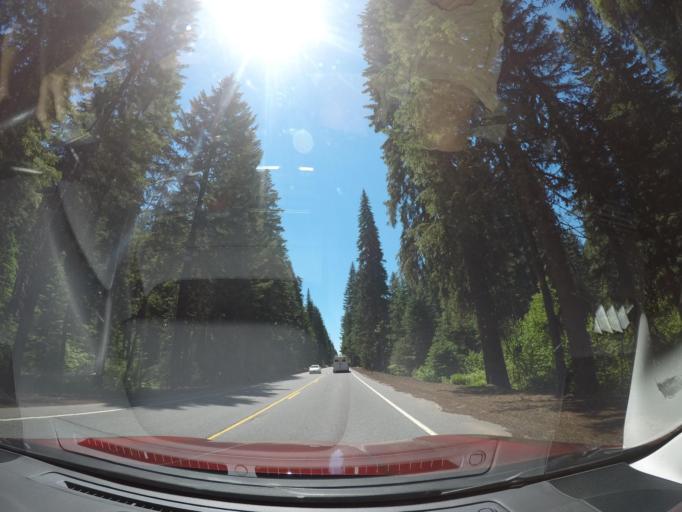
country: US
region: Oregon
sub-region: Deschutes County
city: Sisters
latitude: 44.5367
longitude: -121.9949
